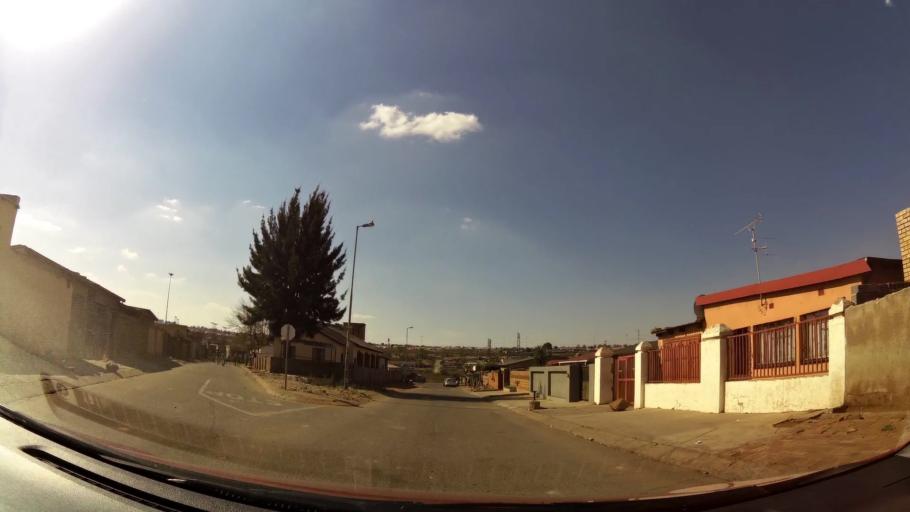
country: ZA
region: Gauteng
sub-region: City of Johannesburg Metropolitan Municipality
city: Soweto
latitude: -26.2346
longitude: 27.8845
